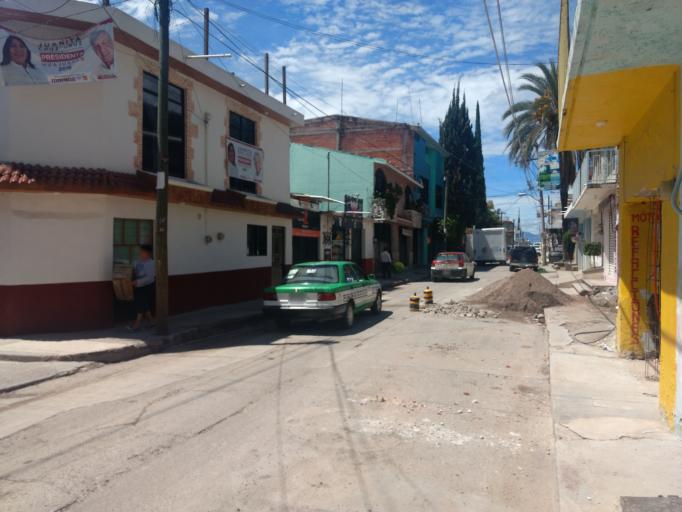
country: MX
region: Oaxaca
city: Ciudad de Huajuapam de Leon
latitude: 17.8101
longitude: -97.7785
